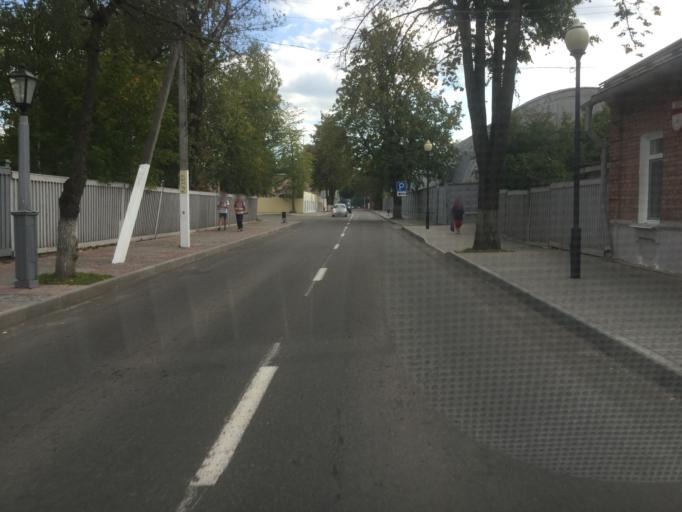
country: BY
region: Vitebsk
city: Vitebsk
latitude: 55.2002
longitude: 30.1905
